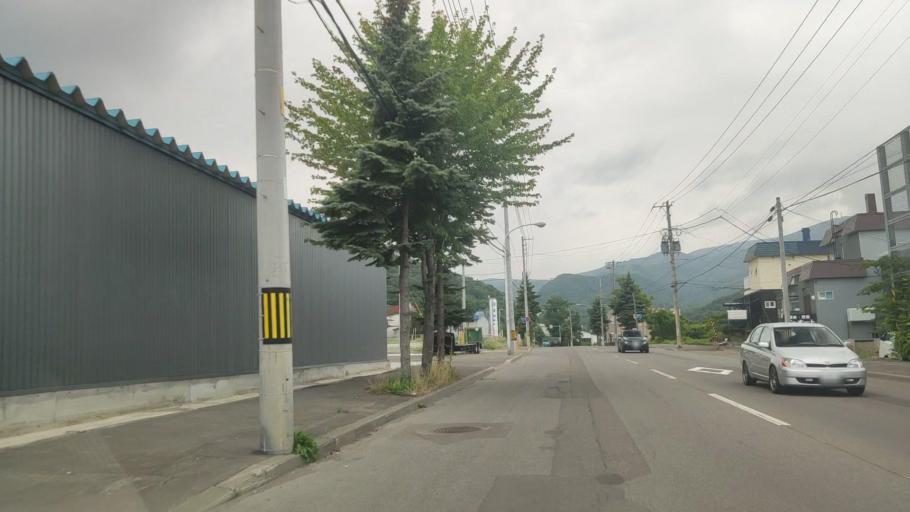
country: JP
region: Hokkaido
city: Otaru
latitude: 43.1642
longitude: 141.0487
